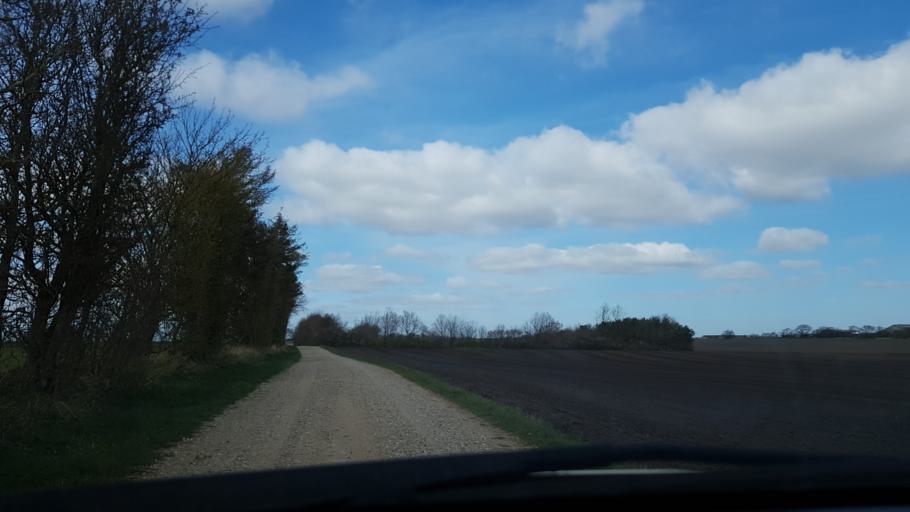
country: DK
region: South Denmark
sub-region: Haderslev Kommune
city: Gram
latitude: 55.2849
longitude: 8.9836
